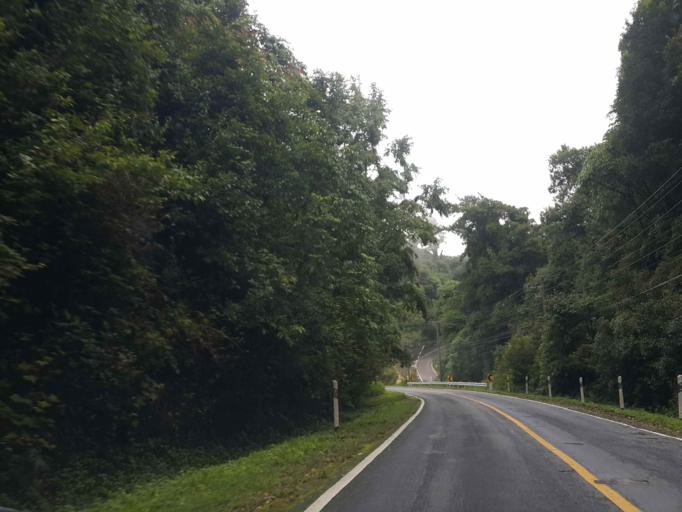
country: TH
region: Chiang Mai
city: Mae Chaem
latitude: 18.5767
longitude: 98.4826
